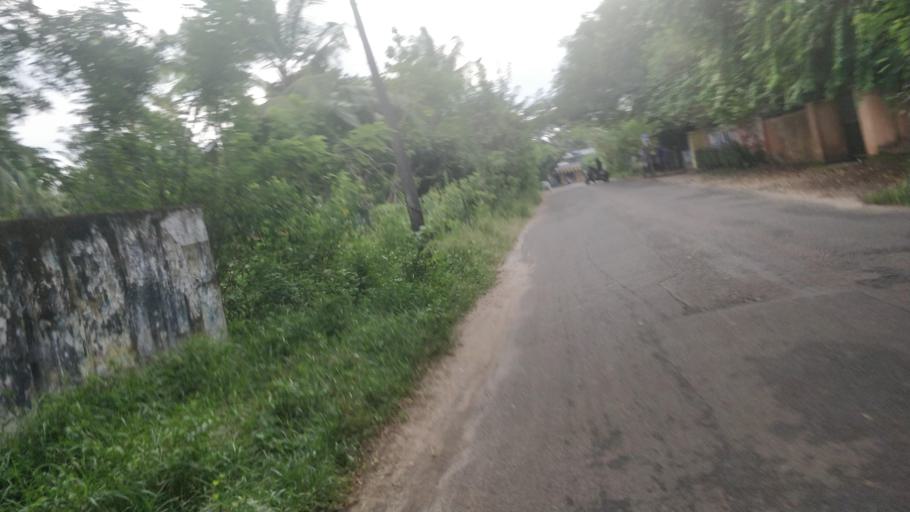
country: IN
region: Kerala
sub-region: Alappuzha
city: Shertallai
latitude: 9.6966
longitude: 76.3571
